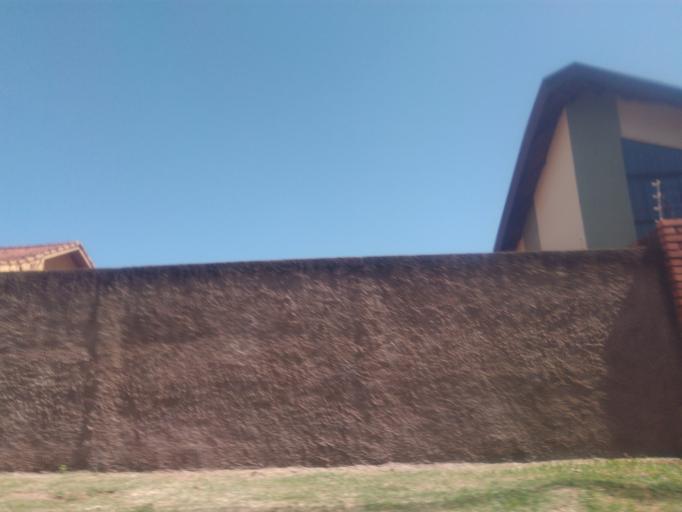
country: BR
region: Mato Grosso do Sul
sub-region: Ponta Pora
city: Ponta Pora
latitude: -22.5209
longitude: -55.7211
